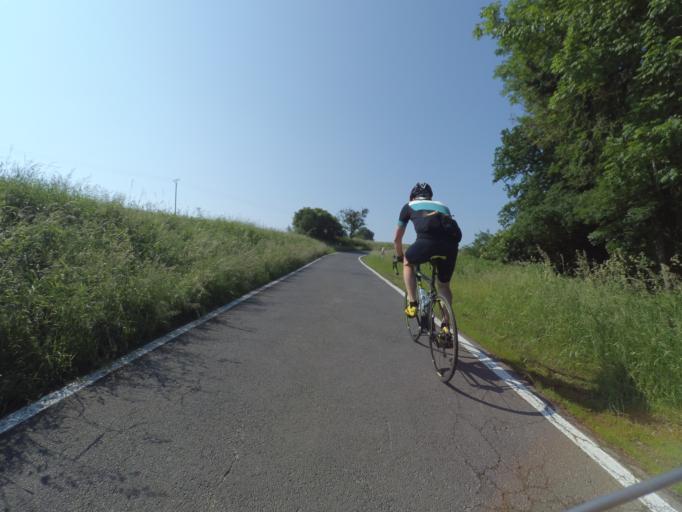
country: DE
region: Rheinland-Pfalz
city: Treis-Karden
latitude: 50.1943
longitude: 7.2999
